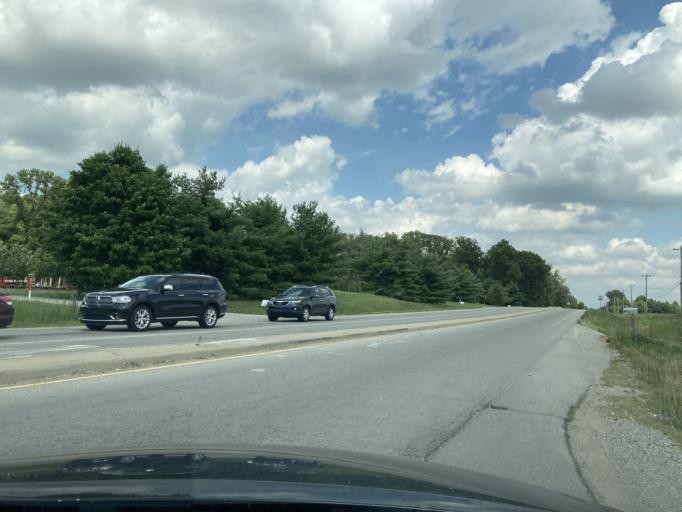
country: US
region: Indiana
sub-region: Boone County
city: Zionsville
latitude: 39.9983
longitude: -86.2643
